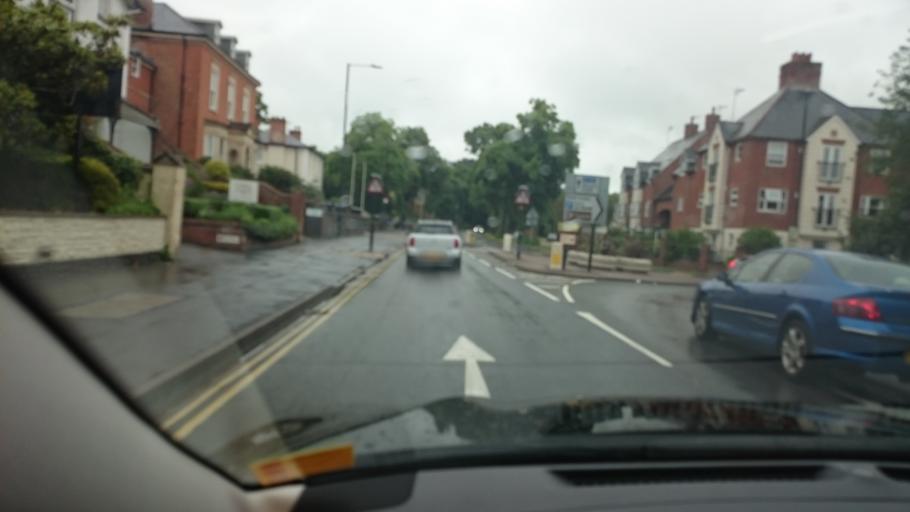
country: GB
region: England
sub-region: Warwickshire
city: Stratford-upon-Avon
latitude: 52.1950
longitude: -1.7025
